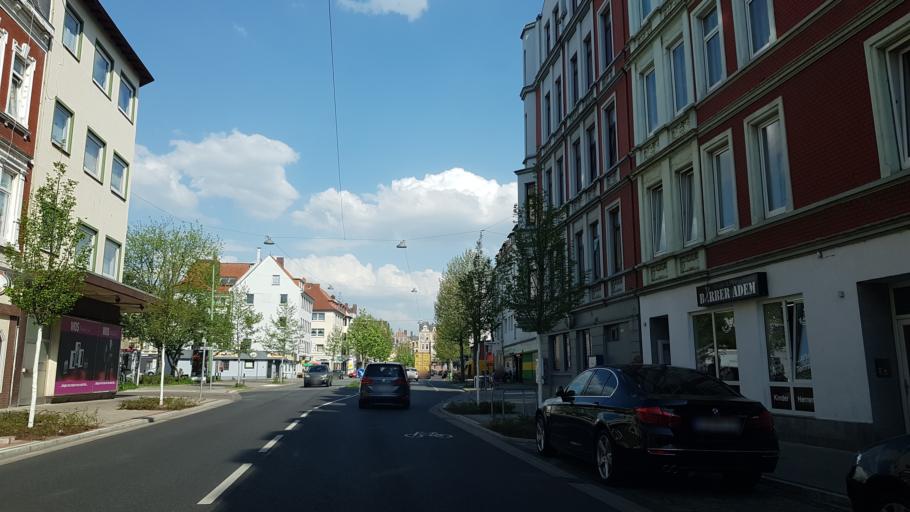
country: DE
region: Bremen
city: Bremerhaven
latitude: 53.5608
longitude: 8.5816
